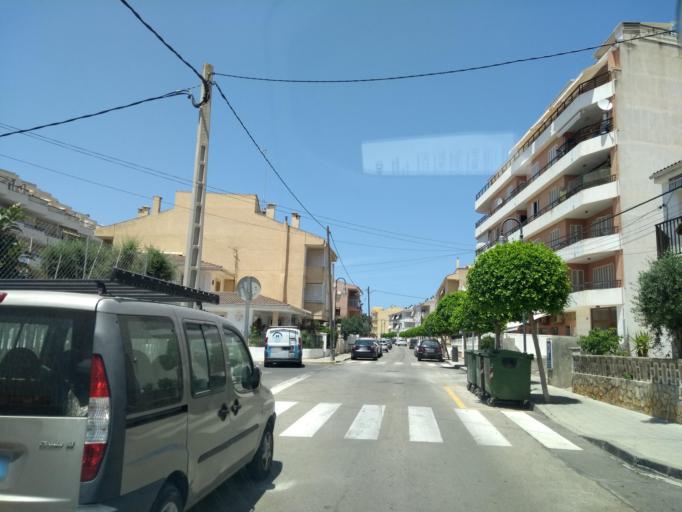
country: ES
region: Balearic Islands
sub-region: Illes Balears
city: Port d'Alcudia
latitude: 39.8396
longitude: 3.1390
